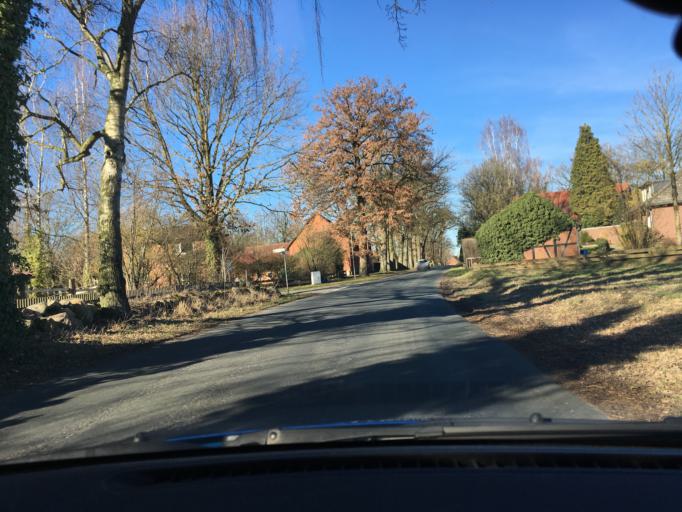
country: DE
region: Lower Saxony
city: Schwienau
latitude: 52.9780
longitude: 10.4457
